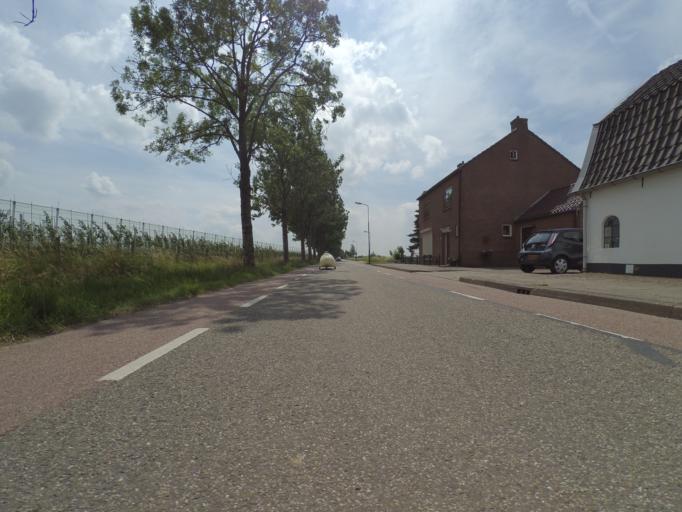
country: NL
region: Utrecht
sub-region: Gemeente Wijk bij Duurstede
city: Wijk bij Duurstede
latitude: 51.9950
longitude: 5.3003
